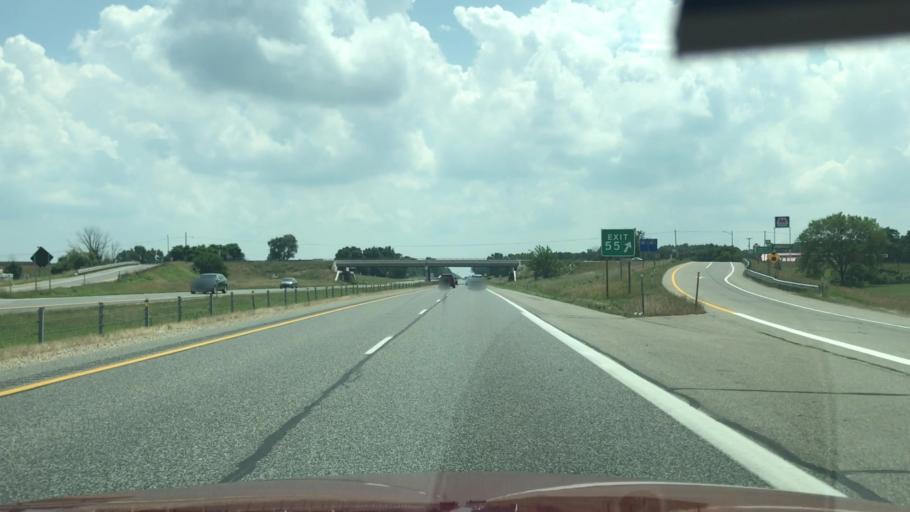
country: US
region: Michigan
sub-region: Allegan County
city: Otsego
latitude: 42.5393
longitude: -85.6607
